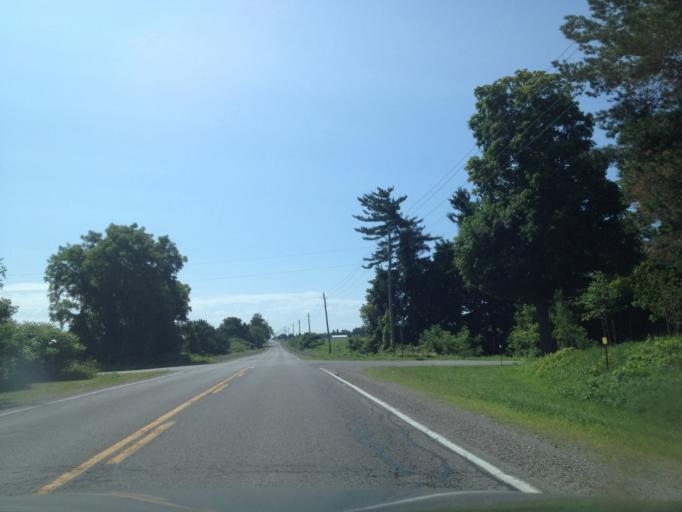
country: CA
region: Ontario
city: Norfolk County
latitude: 42.7540
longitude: -80.3803
